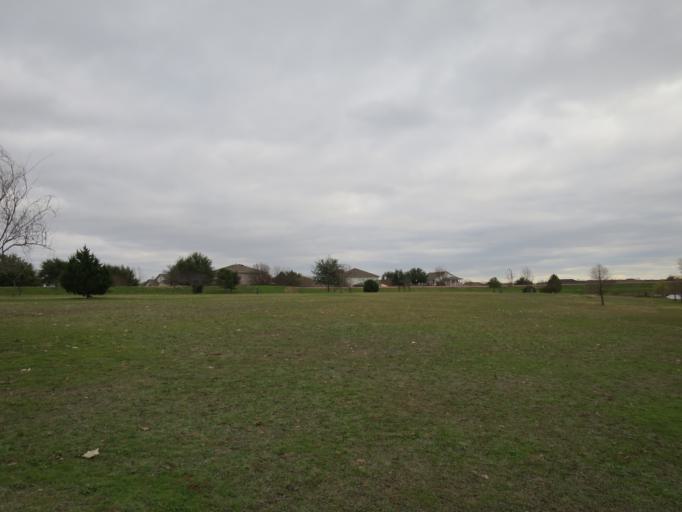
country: US
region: Texas
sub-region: Williamson County
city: Round Rock
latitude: 30.5388
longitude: -97.6251
